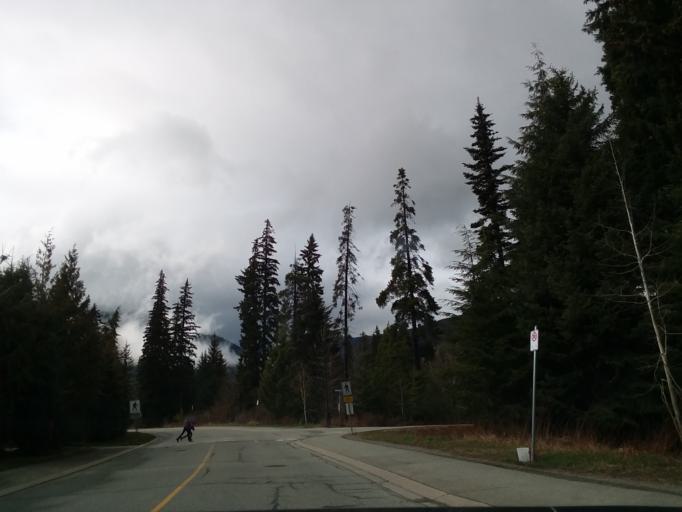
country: CA
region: British Columbia
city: Whistler
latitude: 50.1315
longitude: -122.9501
